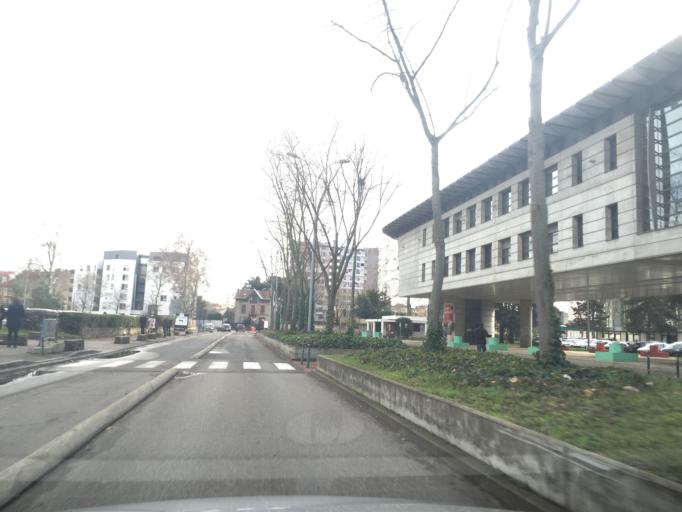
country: FR
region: Rhone-Alpes
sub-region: Departement du Rhone
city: Villeurbanne
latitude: 45.7805
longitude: 4.8719
